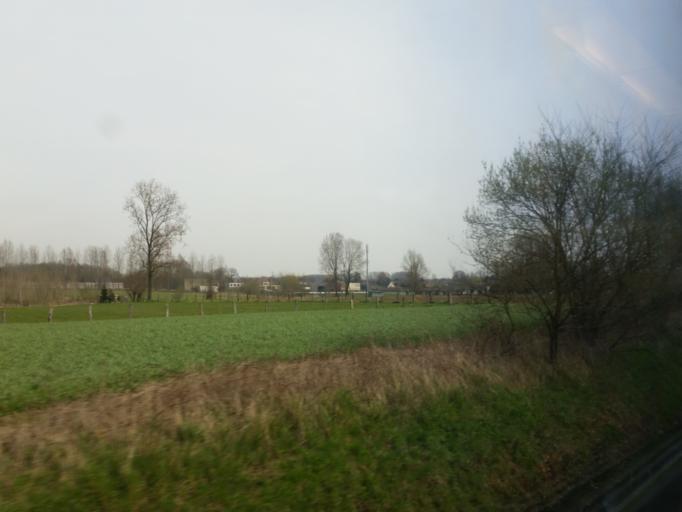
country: BE
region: Flanders
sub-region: Provincie Oost-Vlaanderen
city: Wetteren
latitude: 50.9604
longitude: 3.8823
